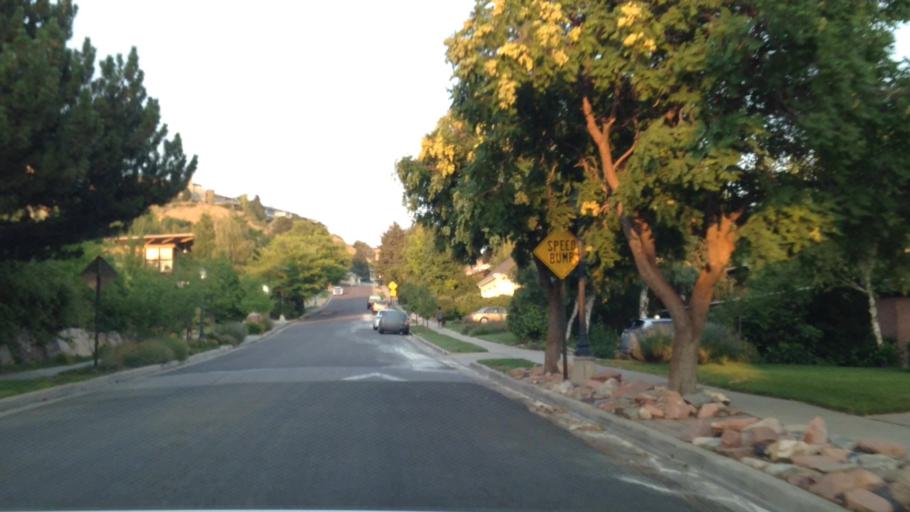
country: US
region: Utah
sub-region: Salt Lake County
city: Salt Lake City
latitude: 40.7890
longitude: -111.8710
